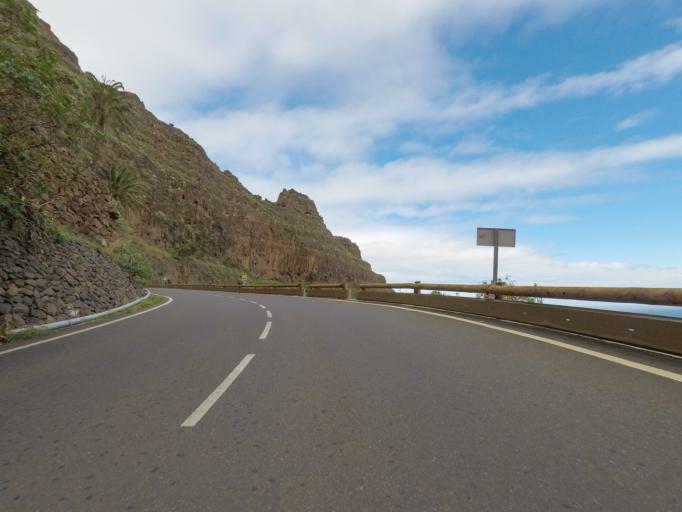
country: ES
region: Canary Islands
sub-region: Provincia de Santa Cruz de Tenerife
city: Agulo
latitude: 28.1879
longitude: -17.1977
